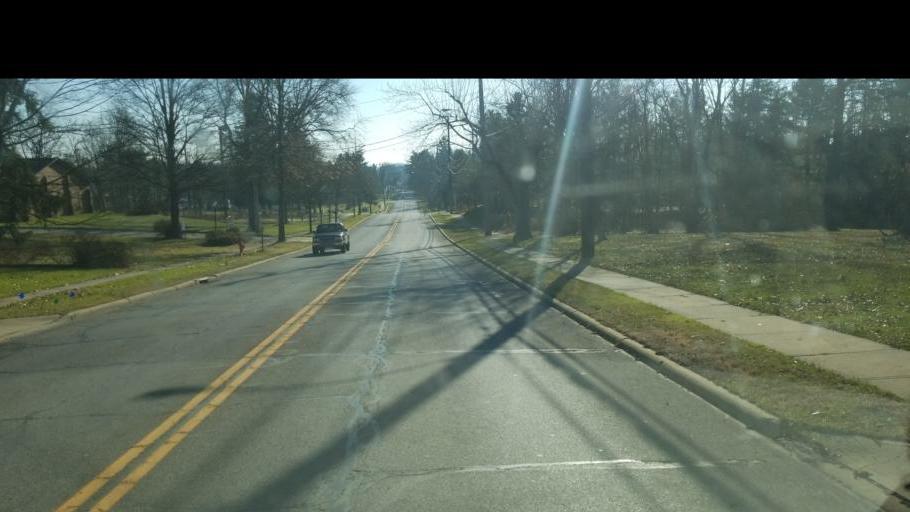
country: US
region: Ohio
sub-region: Geauga County
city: Chardon
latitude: 41.5730
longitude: -81.2035
